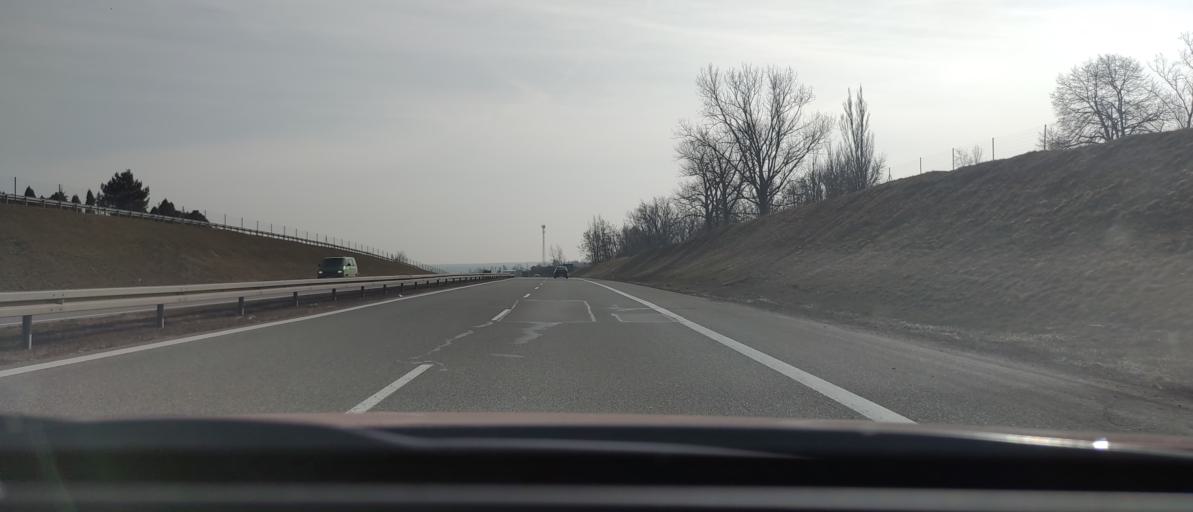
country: PL
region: Masovian Voivodeship
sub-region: Powiat bialobrzeski
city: Promna
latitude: 51.6825
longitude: 20.9377
